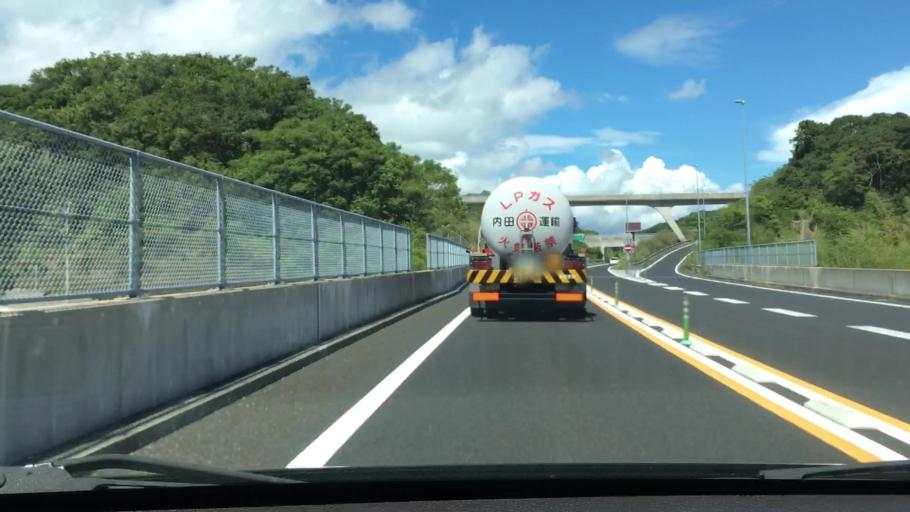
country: JP
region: Nagasaki
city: Sasebo
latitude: 33.0417
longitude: 129.7465
